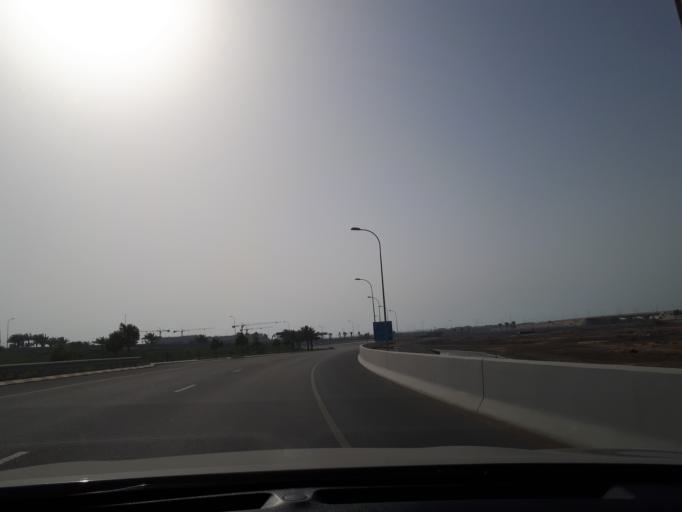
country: OM
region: Muhafazat Masqat
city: Bawshar
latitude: 23.6037
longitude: 58.3151
